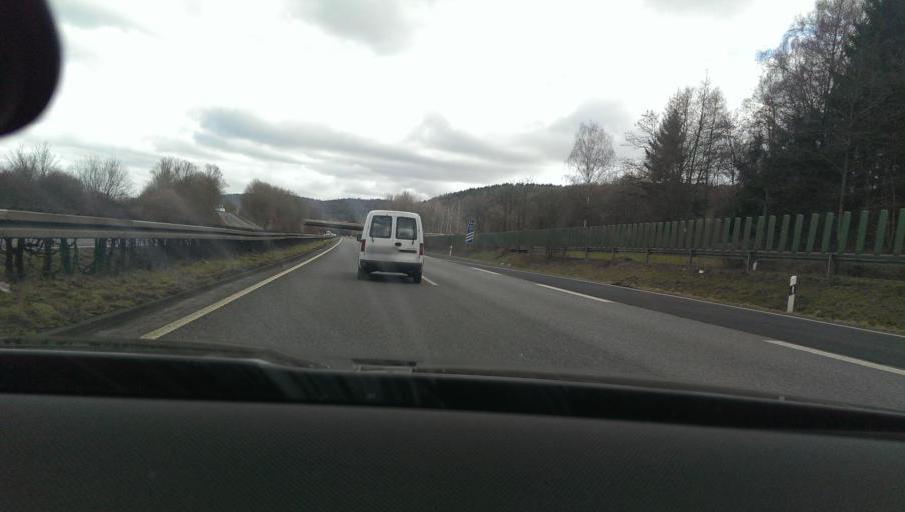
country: DE
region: Hesse
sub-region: Regierungsbezirk Darmstadt
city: Gelnhausen
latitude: 50.1967
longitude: 9.2145
